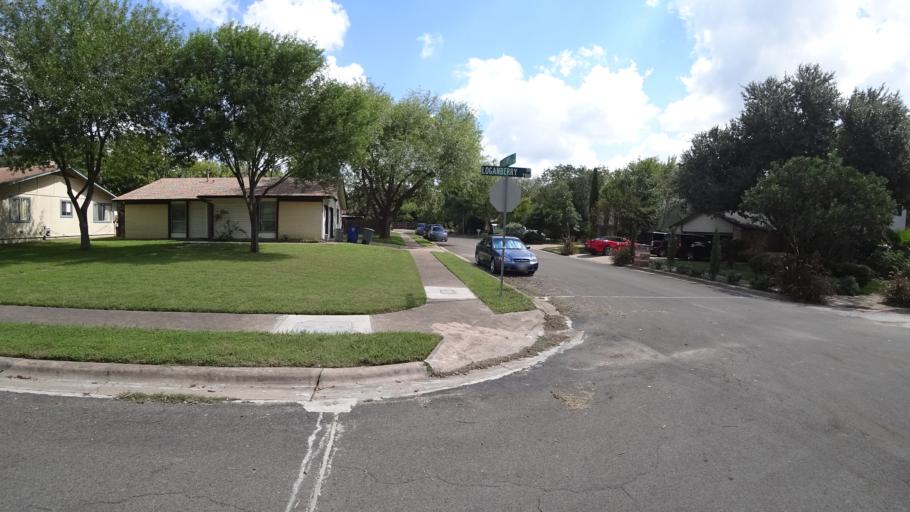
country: US
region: Texas
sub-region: Travis County
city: Onion Creek
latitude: 30.1858
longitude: -97.7859
